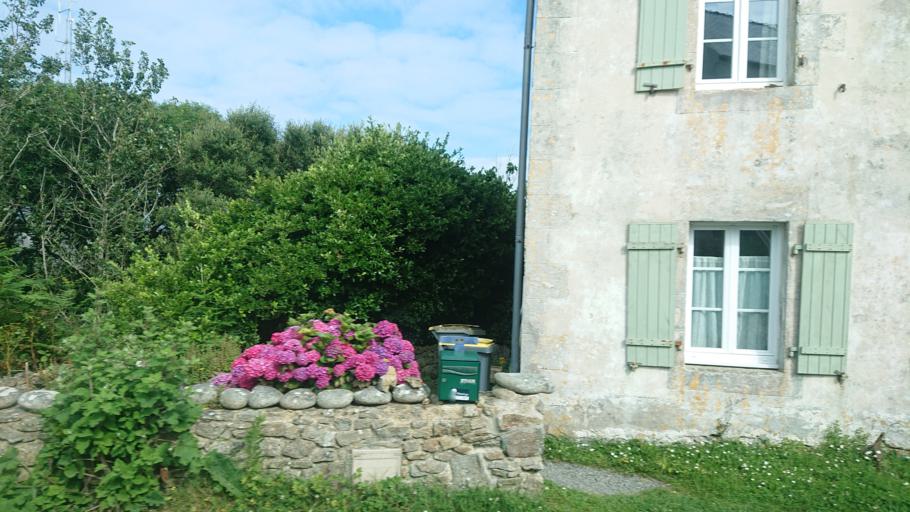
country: FR
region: Brittany
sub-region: Departement du Finistere
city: Porspoder
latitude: 48.4597
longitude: -5.0911
